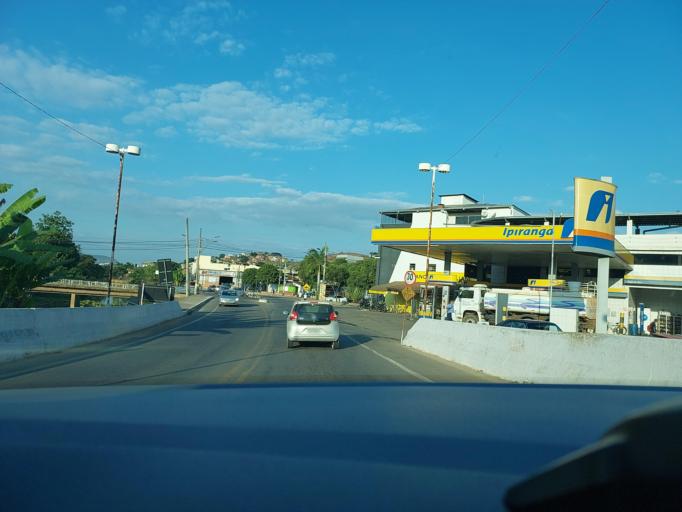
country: BR
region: Minas Gerais
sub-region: Muriae
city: Muriae
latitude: -21.1303
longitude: -42.3949
